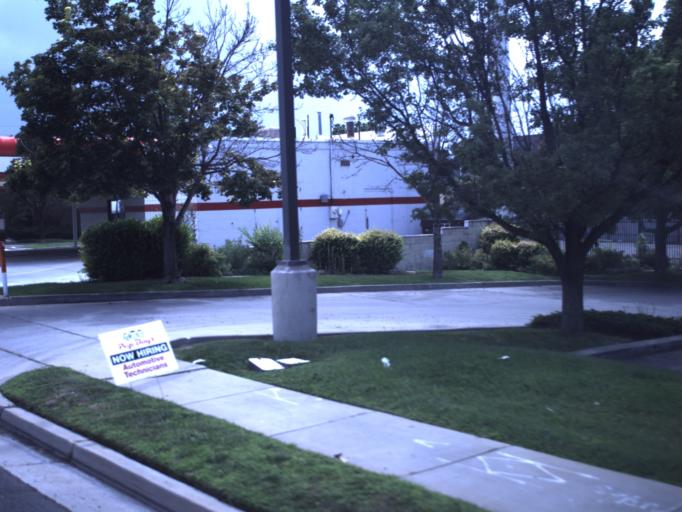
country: US
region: Utah
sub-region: Salt Lake County
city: South Salt Lake
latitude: 40.7240
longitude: -111.8714
